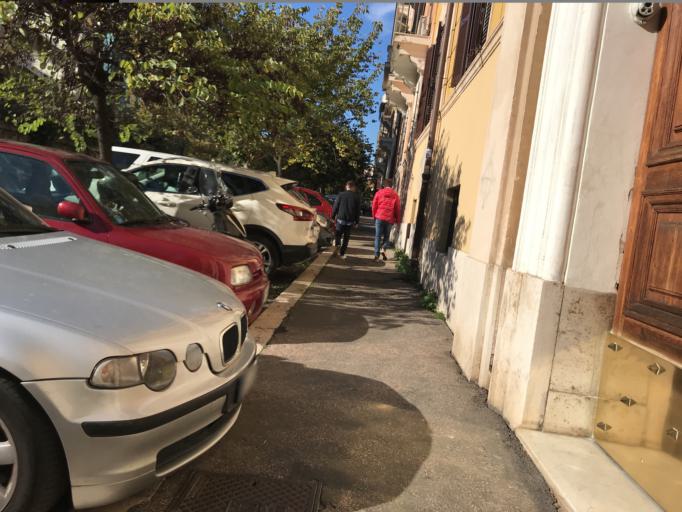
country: IT
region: Latium
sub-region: Citta metropolitana di Roma Capitale
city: Rome
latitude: 41.9081
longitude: 12.5146
